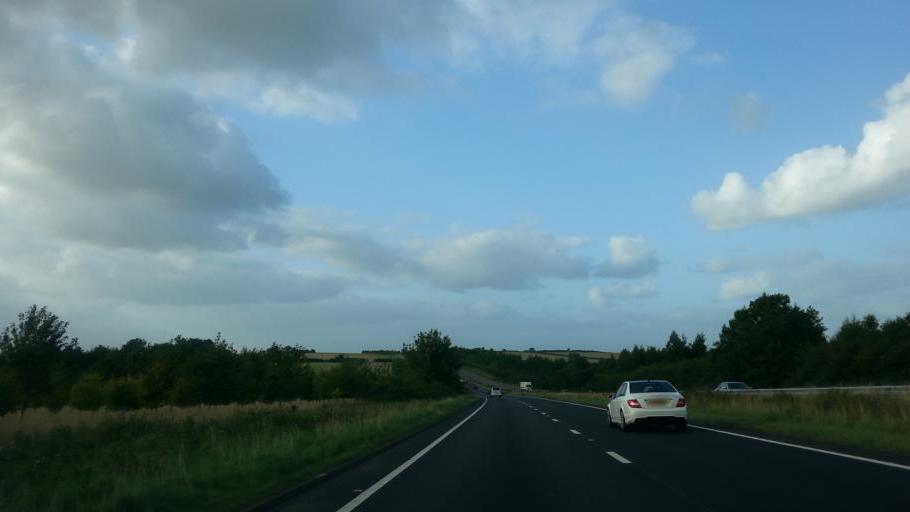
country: GB
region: England
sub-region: Hampshire
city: Overton
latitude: 51.1963
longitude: -1.3369
